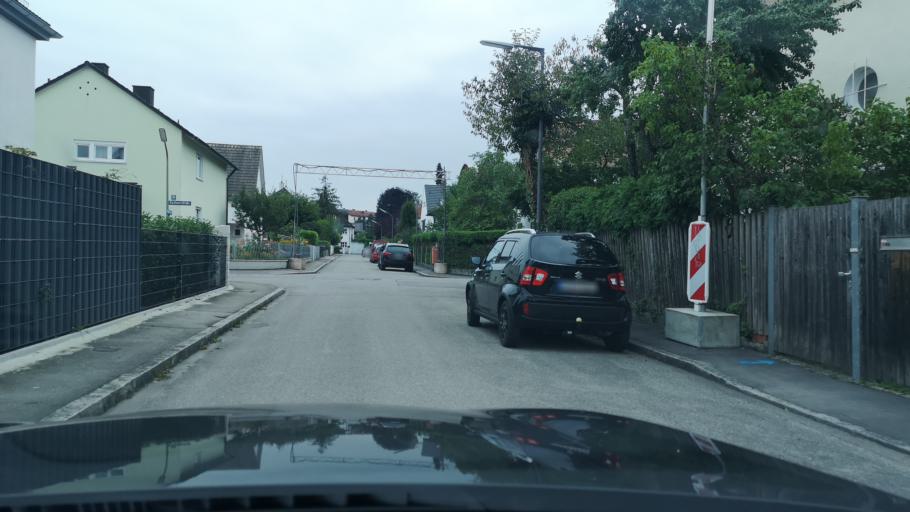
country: DE
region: Bavaria
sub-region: Upper Bavaria
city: Pasing
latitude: 48.1309
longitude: 11.5139
